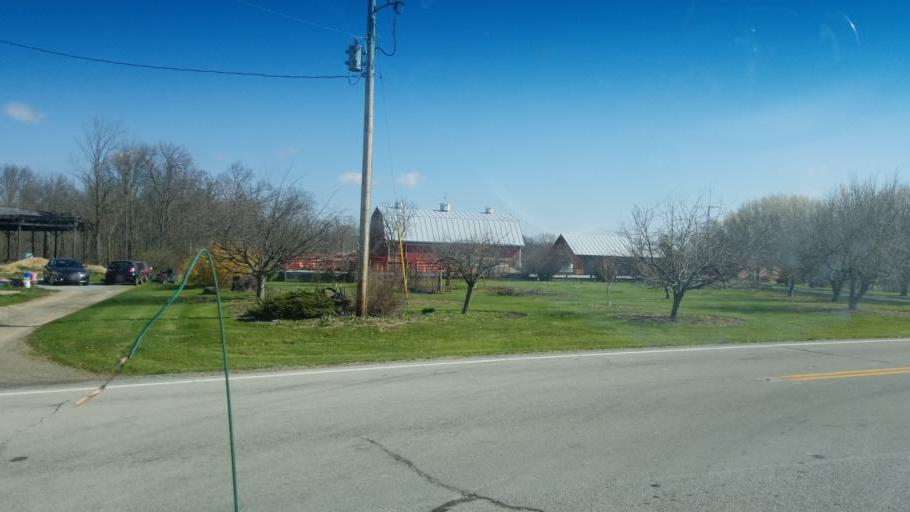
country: US
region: Ohio
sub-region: Hardin County
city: Forest
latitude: 40.7374
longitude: -83.4003
